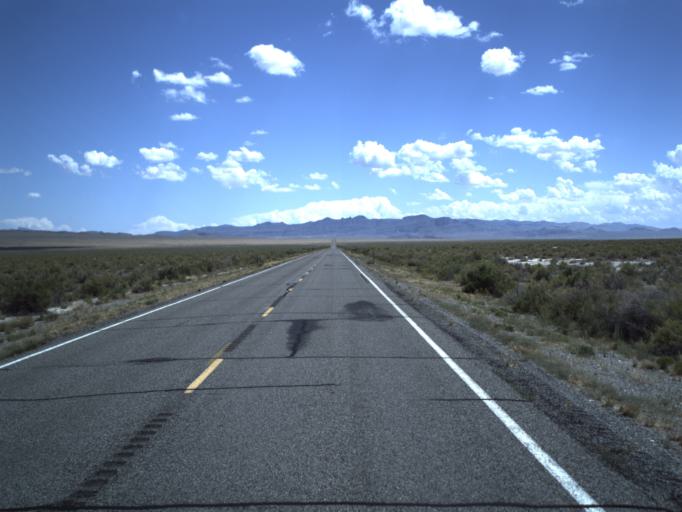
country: US
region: Nevada
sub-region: White Pine County
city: McGill
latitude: 39.0475
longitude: -113.9227
